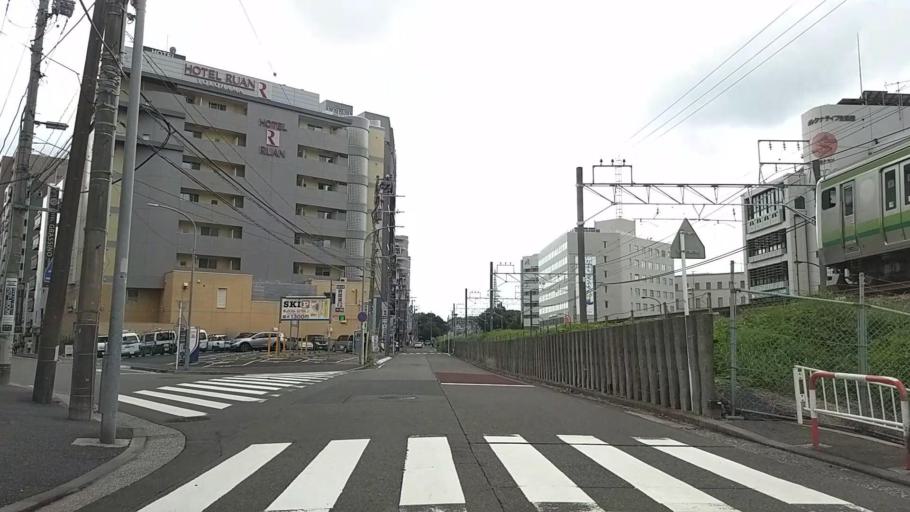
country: JP
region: Kanagawa
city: Yokohama
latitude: 35.5061
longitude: 139.6122
